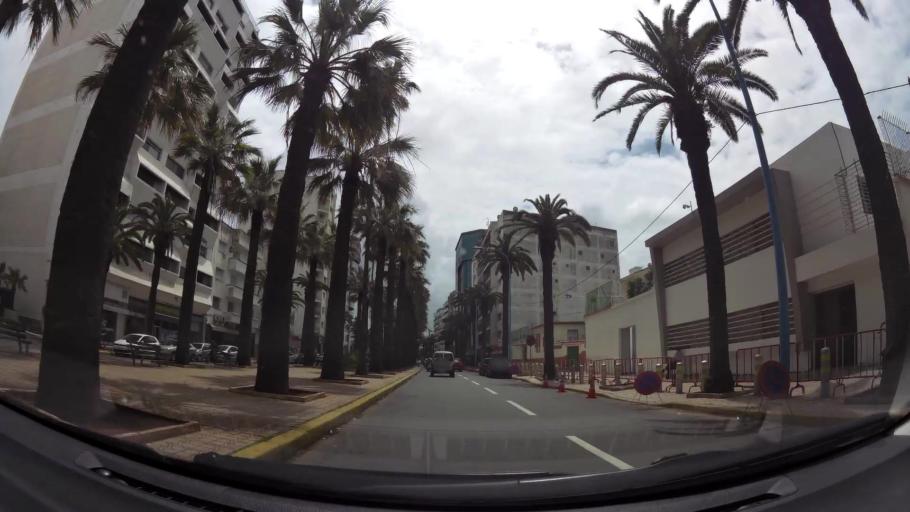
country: MA
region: Grand Casablanca
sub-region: Casablanca
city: Casablanca
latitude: 33.5955
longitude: -7.6303
